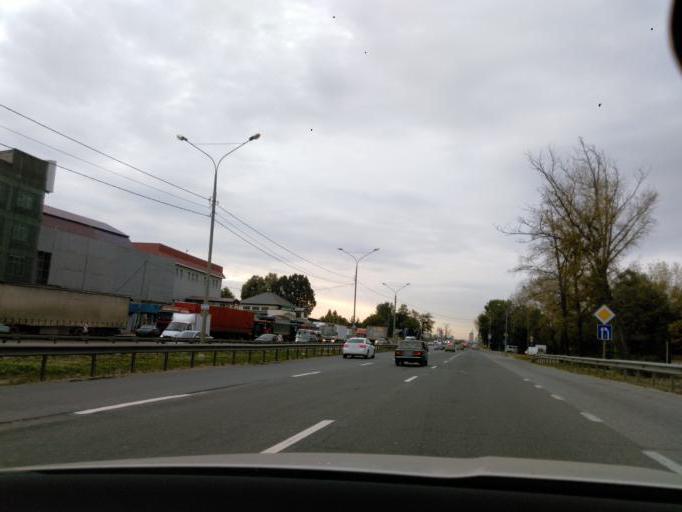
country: RU
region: Moscow
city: Severnyy
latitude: 55.9580
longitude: 37.5337
